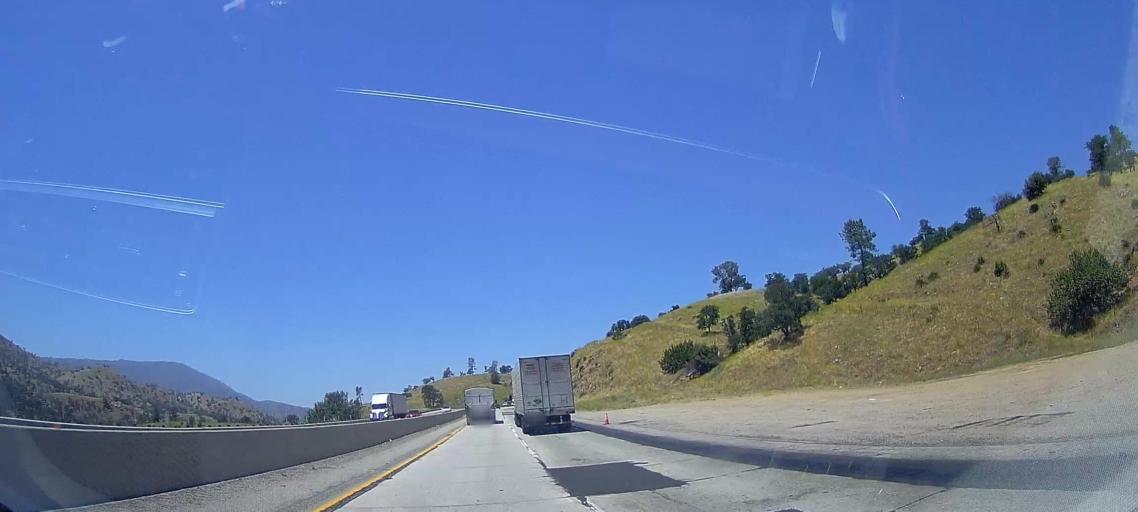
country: US
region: California
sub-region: Kern County
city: Golden Hills
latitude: 35.1848
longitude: -118.5010
